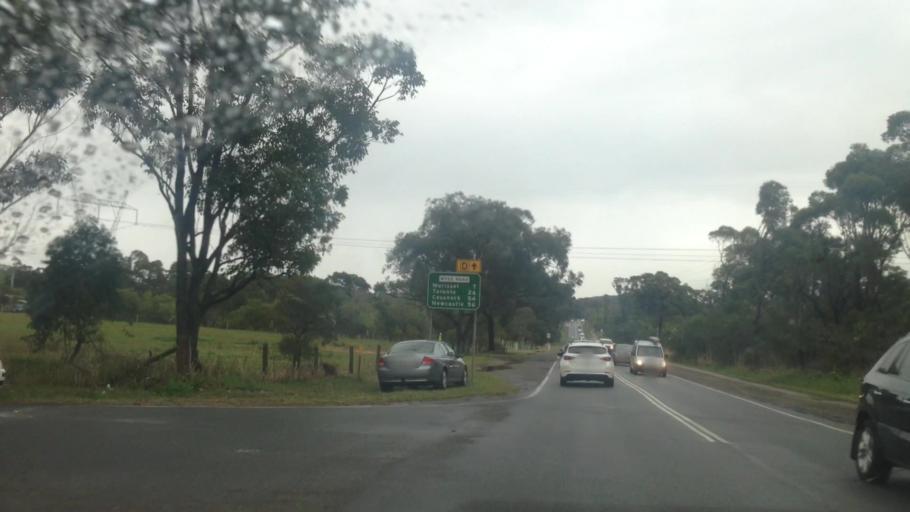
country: AU
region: New South Wales
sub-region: Wyong Shire
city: Charmhaven
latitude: -33.1745
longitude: 151.4798
